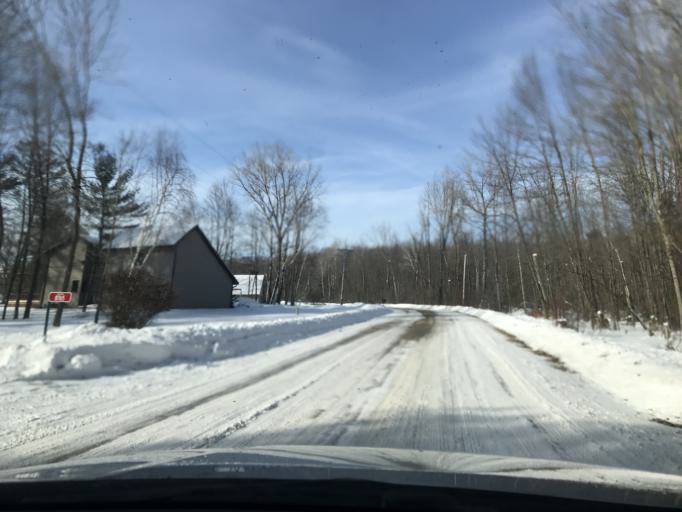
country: US
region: Wisconsin
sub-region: Oconto County
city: Oconto Falls
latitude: 45.1560
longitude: -88.1939
